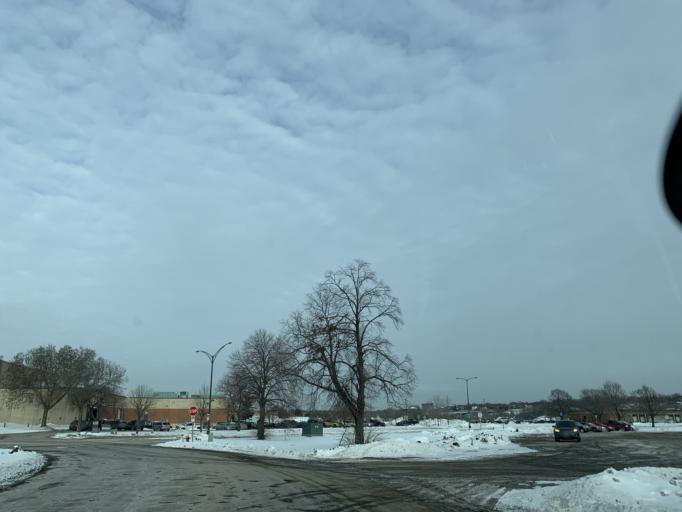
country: US
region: Minnesota
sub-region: Ramsey County
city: Saint Paul
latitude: 44.9405
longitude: -93.0725
